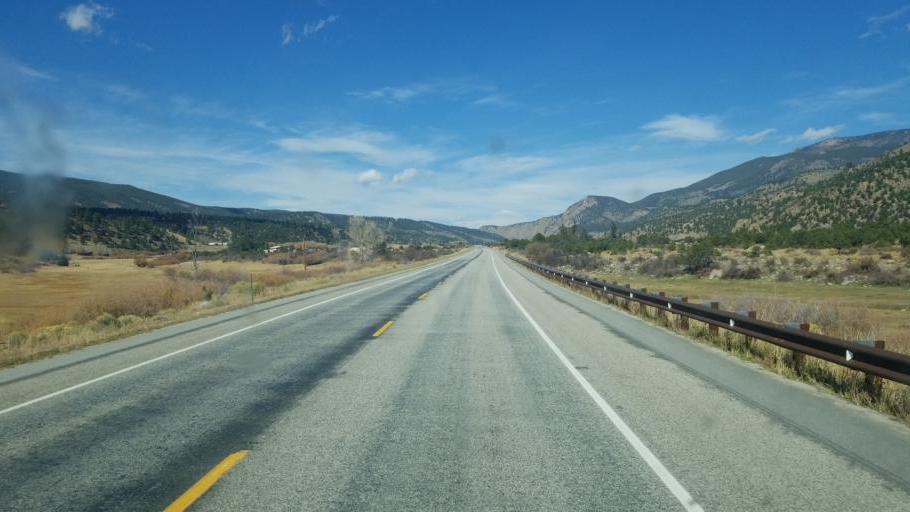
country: US
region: Colorado
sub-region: Chaffee County
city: Buena Vista
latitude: 38.9401
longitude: -106.1900
